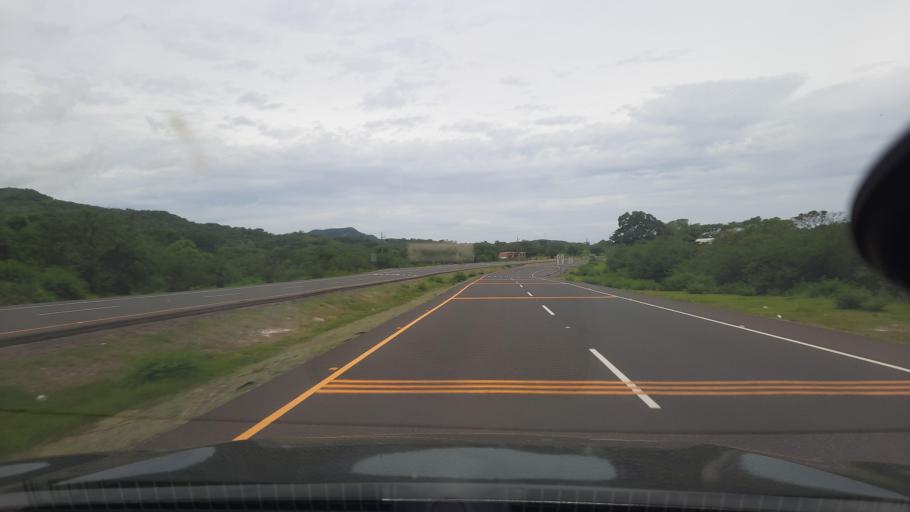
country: HN
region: Valle
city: Aramecina
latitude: 13.7115
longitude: -87.7065
